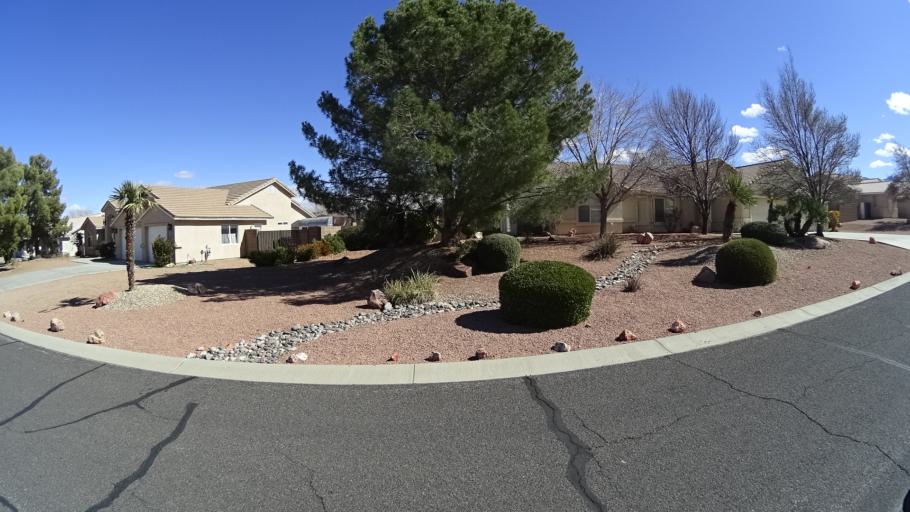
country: US
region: Arizona
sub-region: Mohave County
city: Kingman
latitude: 35.2051
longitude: -113.9718
